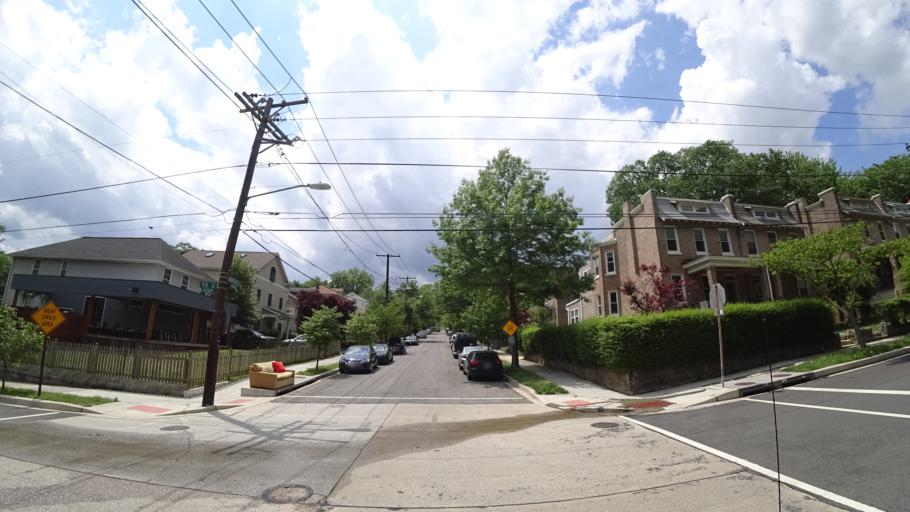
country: US
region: Maryland
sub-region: Prince George's County
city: Mount Rainier
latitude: 38.9319
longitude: -76.9843
